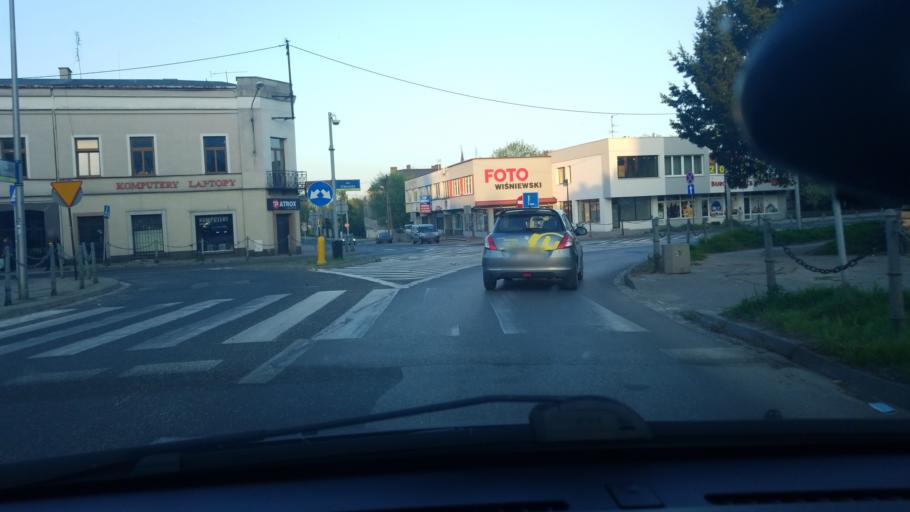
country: PL
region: Silesian Voivodeship
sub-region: Czestochowa
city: Czestochowa
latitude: 50.8099
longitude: 19.1274
